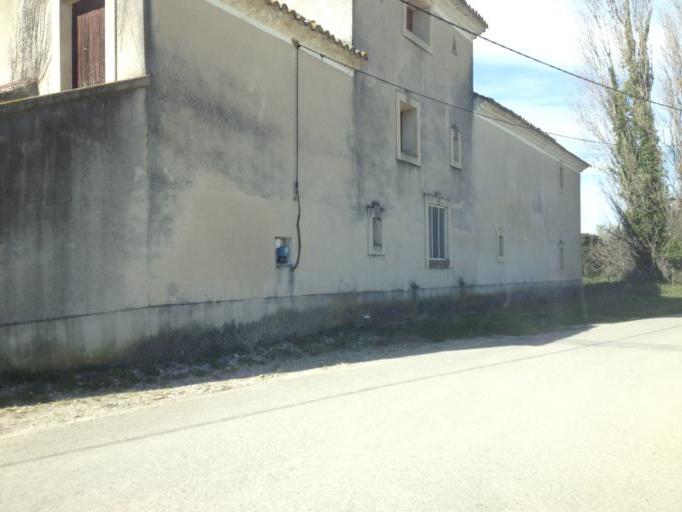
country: FR
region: Provence-Alpes-Cote d'Azur
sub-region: Departement du Vaucluse
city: Caderousse
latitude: 44.1018
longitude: 4.7351
